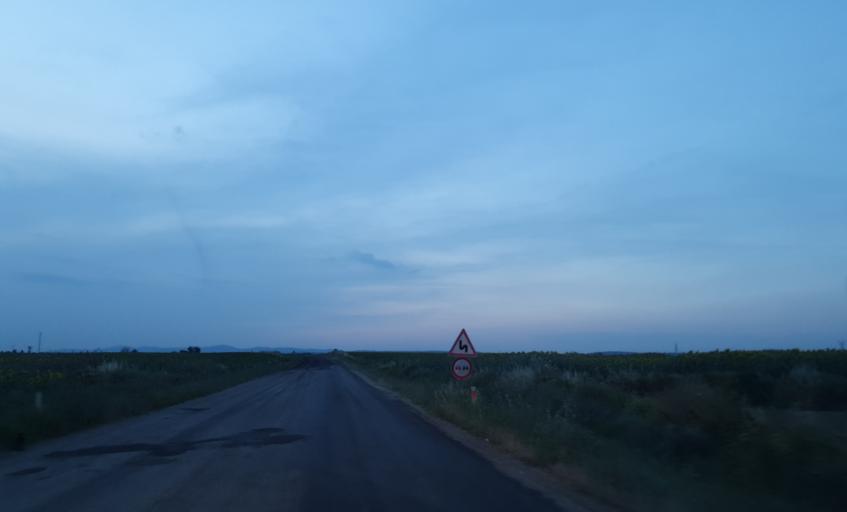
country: TR
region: Kirklareli
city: Vize
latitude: 41.5040
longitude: 27.7509
